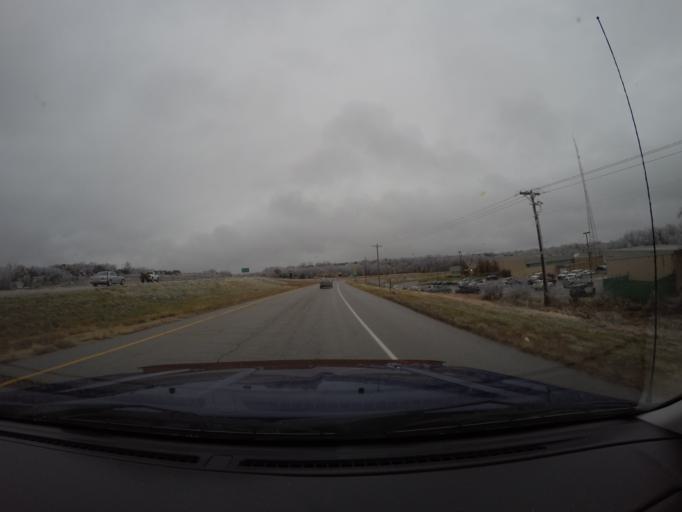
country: US
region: Kansas
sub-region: Riley County
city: Manhattan
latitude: 39.1692
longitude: -96.6012
